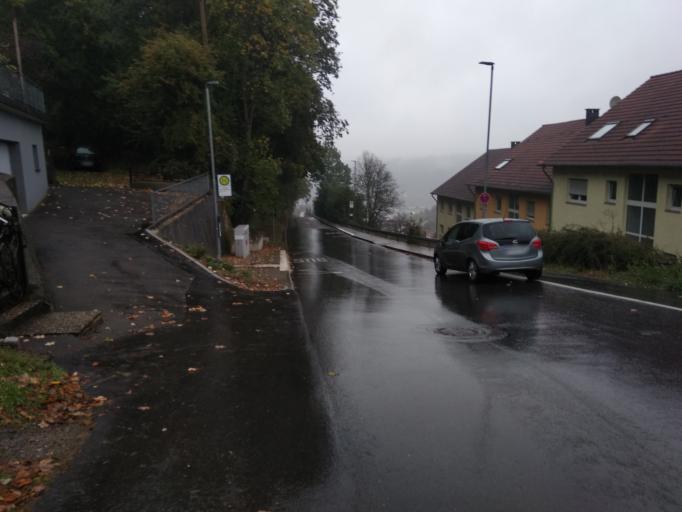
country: DE
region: Baden-Wuerttemberg
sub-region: Karlsruhe Region
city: Mosbach
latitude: 49.3496
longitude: 9.1648
